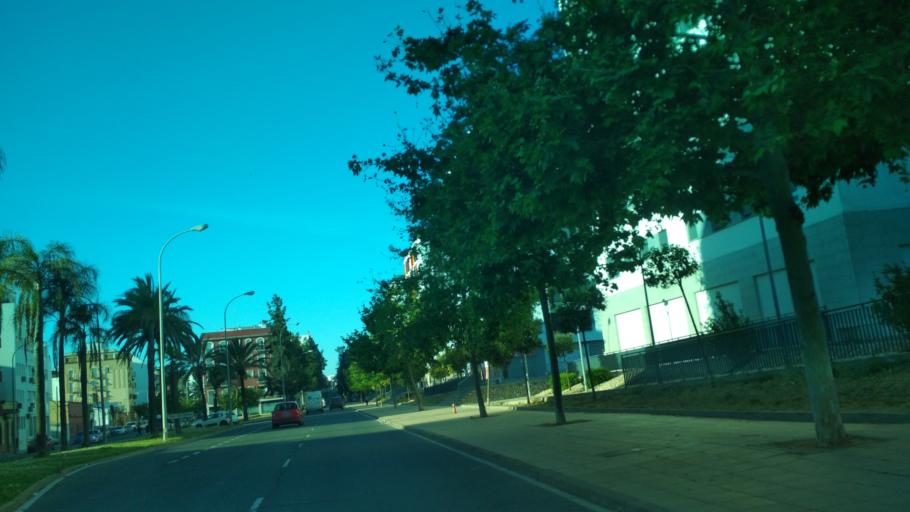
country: ES
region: Andalusia
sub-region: Provincia de Huelva
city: Huelva
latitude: 37.2752
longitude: -6.9495
